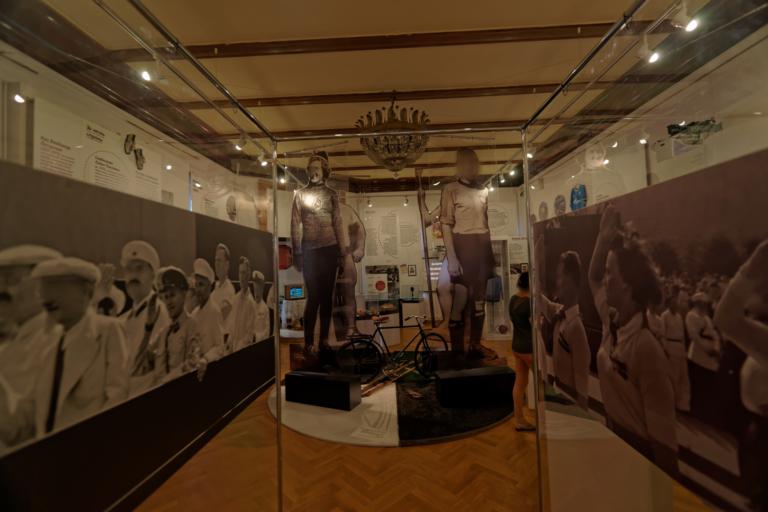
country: RU
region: St.-Petersburg
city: Petrogradka
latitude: 59.9544
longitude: 30.3244
